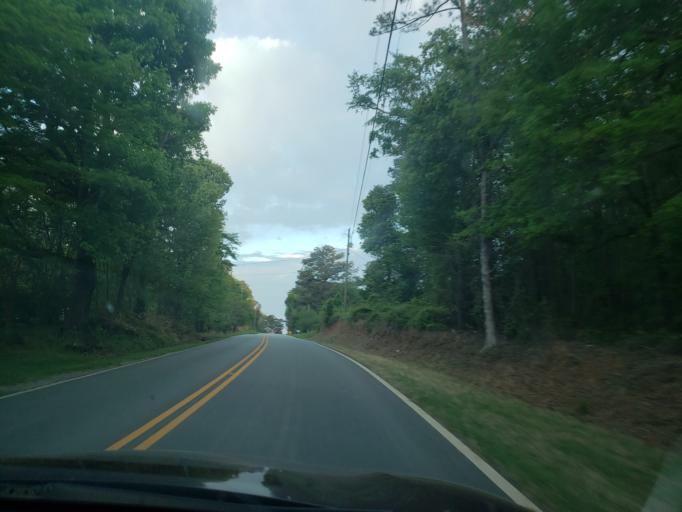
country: US
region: Alabama
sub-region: Tallapoosa County
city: Dadeville
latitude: 32.7024
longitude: -85.7517
